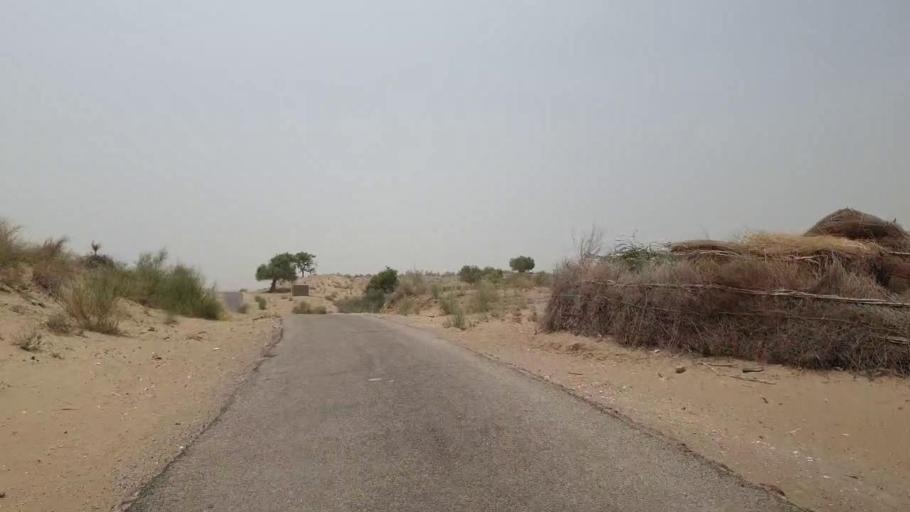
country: PK
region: Sindh
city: Islamkot
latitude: 24.7878
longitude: 70.5111
